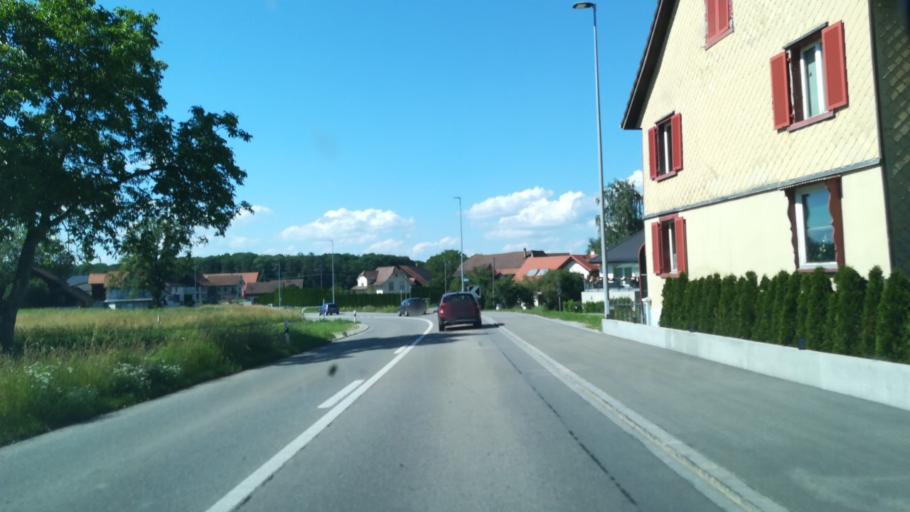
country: CH
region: Thurgau
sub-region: Kreuzlingen District
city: Kreuzlingen
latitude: 47.6292
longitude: 9.1670
